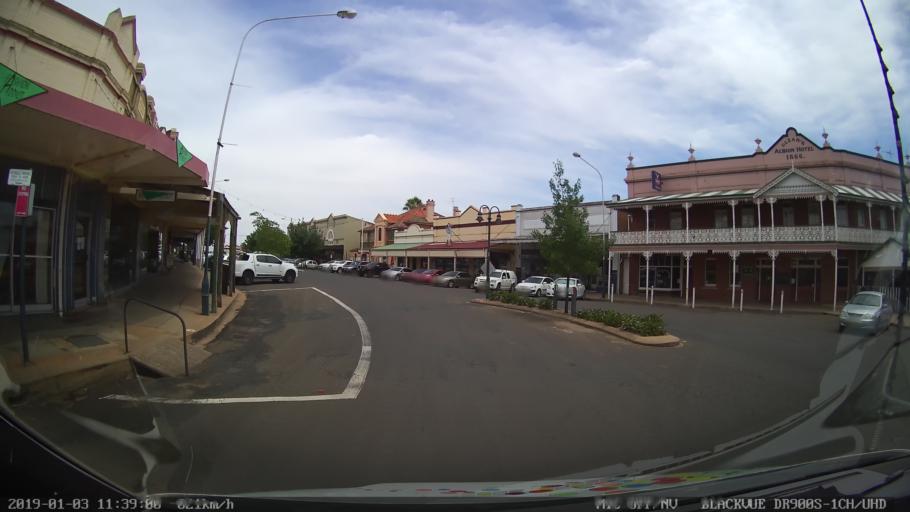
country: AU
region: New South Wales
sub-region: Weddin
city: Grenfell
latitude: -33.8941
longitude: 148.1624
